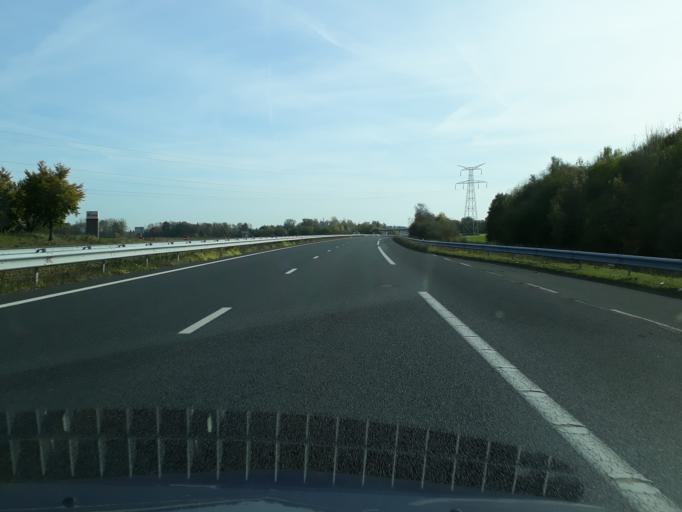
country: FR
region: Champagne-Ardenne
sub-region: Departement de l'Aube
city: Saint-Pouange
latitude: 48.2319
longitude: 4.0532
